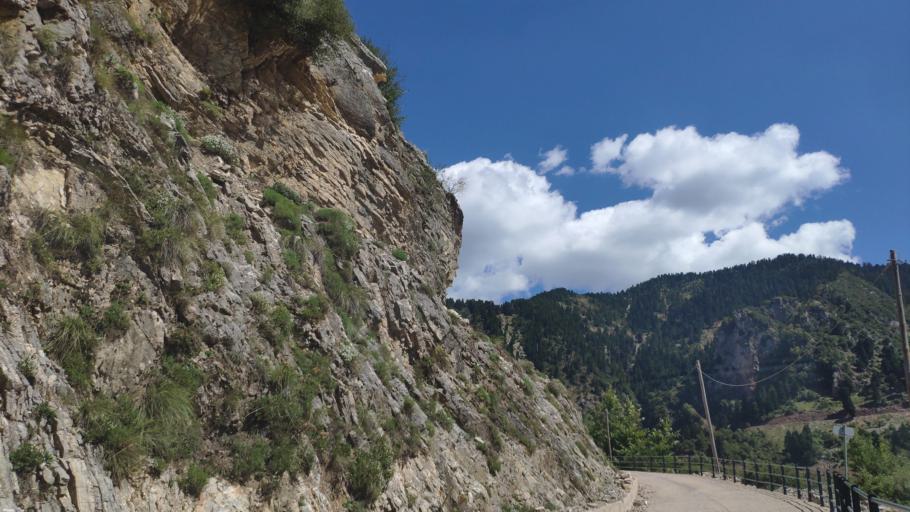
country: GR
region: Central Greece
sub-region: Nomos Evrytanias
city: Kerasochori
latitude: 39.1368
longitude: 21.6512
